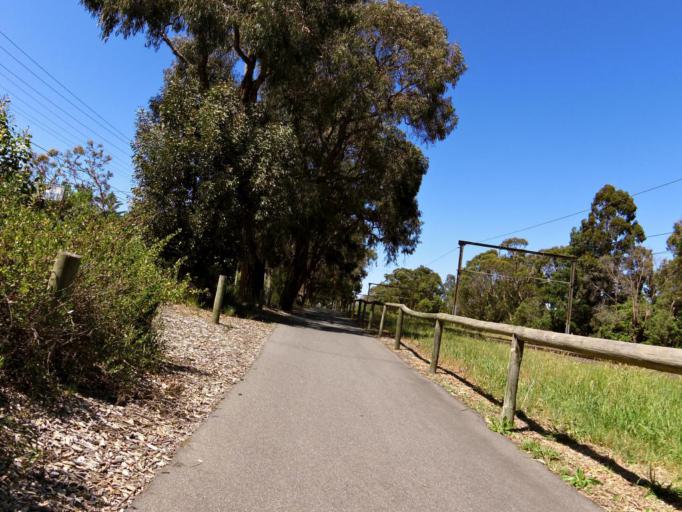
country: AU
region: Victoria
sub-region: Knox
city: Ferntree Gully
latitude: -37.8756
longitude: 145.2923
